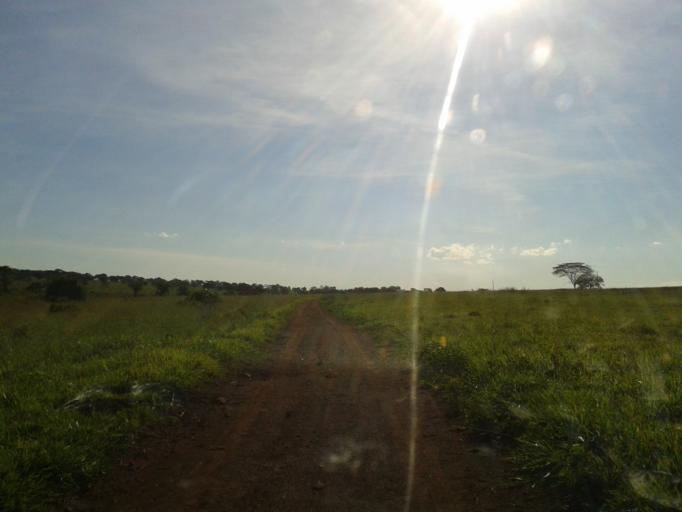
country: BR
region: Minas Gerais
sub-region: Santa Vitoria
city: Santa Vitoria
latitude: -19.0006
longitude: -50.3450
